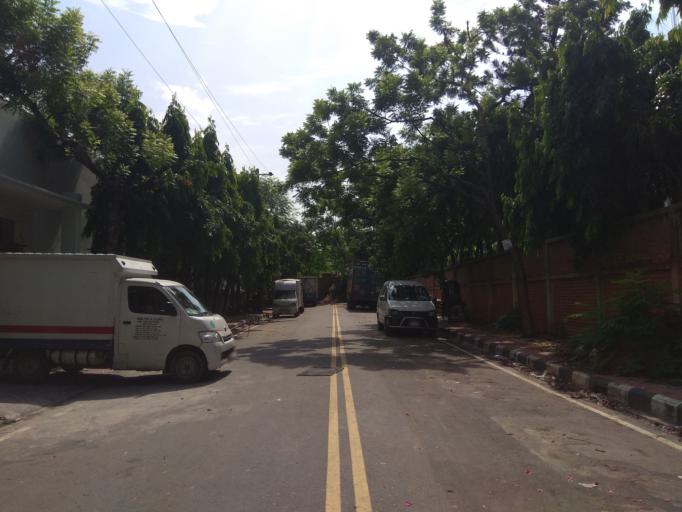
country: BD
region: Dhaka
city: Azimpur
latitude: 23.8105
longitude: 90.3587
